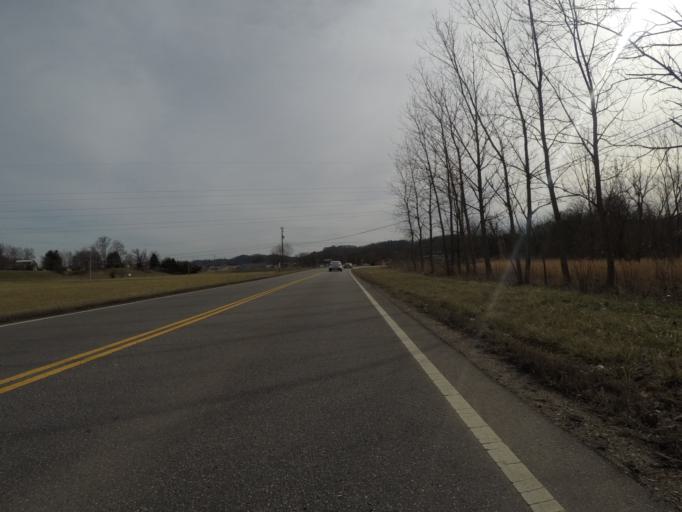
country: US
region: West Virginia
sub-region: Cabell County
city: Pea Ridge
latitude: 38.4408
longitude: -82.3708
